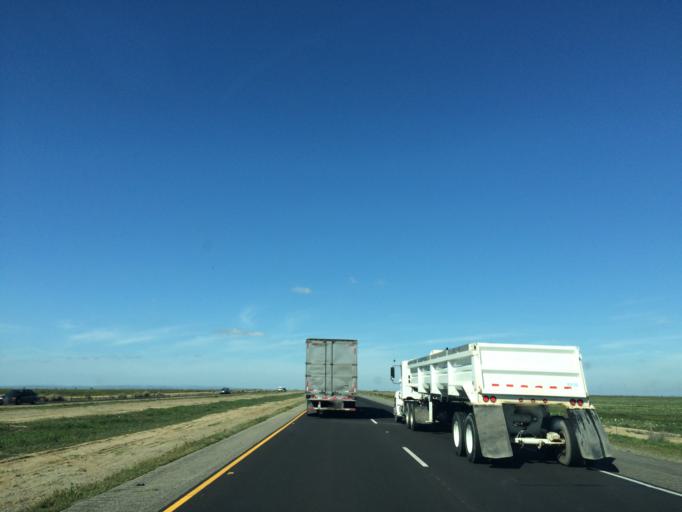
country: US
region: California
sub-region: Kern County
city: Lost Hills
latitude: 35.7652
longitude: -119.7640
